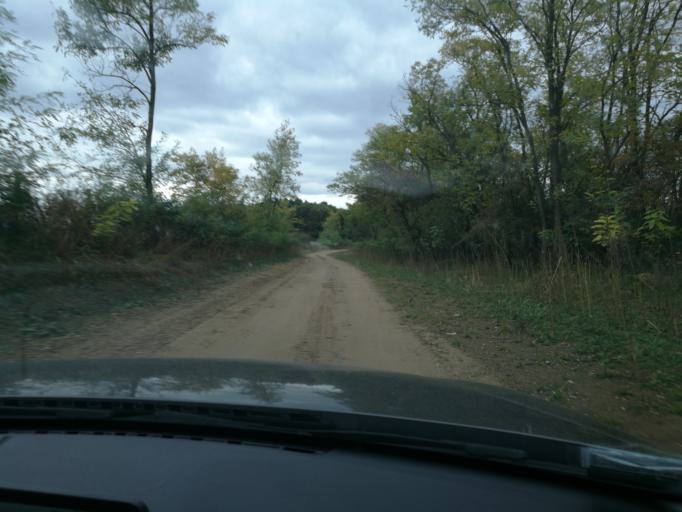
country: HU
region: Szabolcs-Szatmar-Bereg
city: Nyirpazony
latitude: 47.9947
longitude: 21.7882
